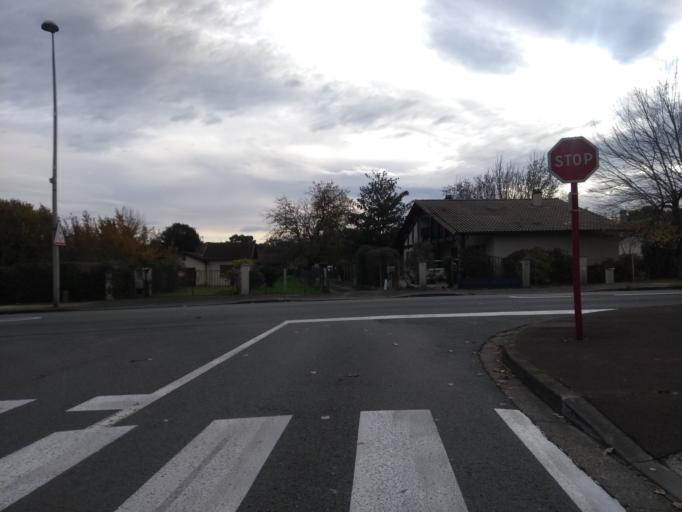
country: FR
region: Aquitaine
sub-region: Departement de la Gironde
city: Canejan
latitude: 44.7625
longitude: -0.6530
